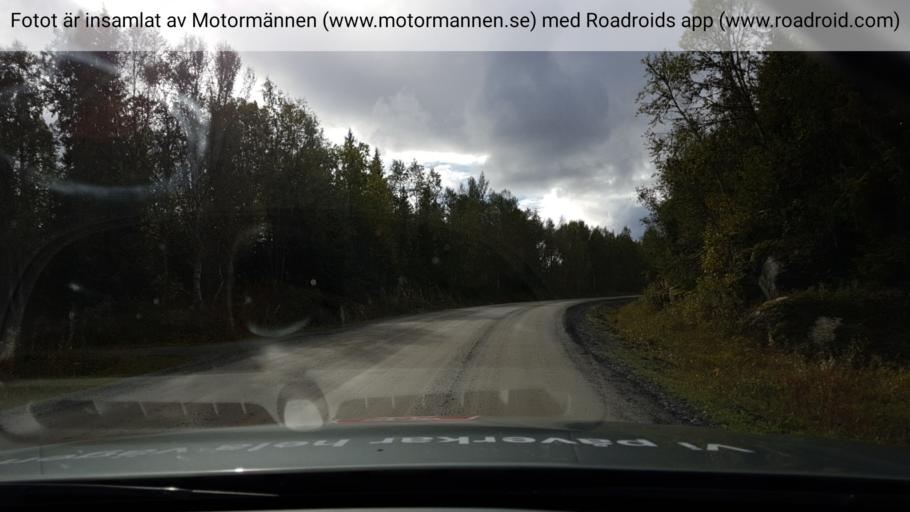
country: SE
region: Jaemtland
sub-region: Are Kommun
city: Are
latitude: 63.6882
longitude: 12.8104
